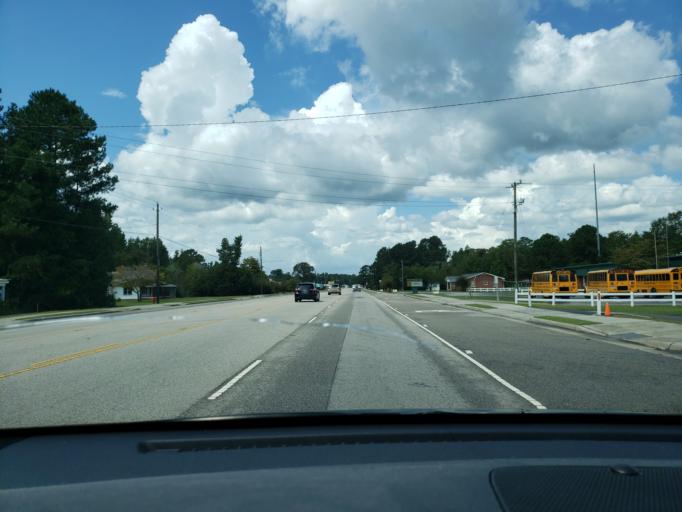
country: US
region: North Carolina
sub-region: Bladen County
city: Elizabethtown
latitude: 34.6544
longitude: -78.7192
